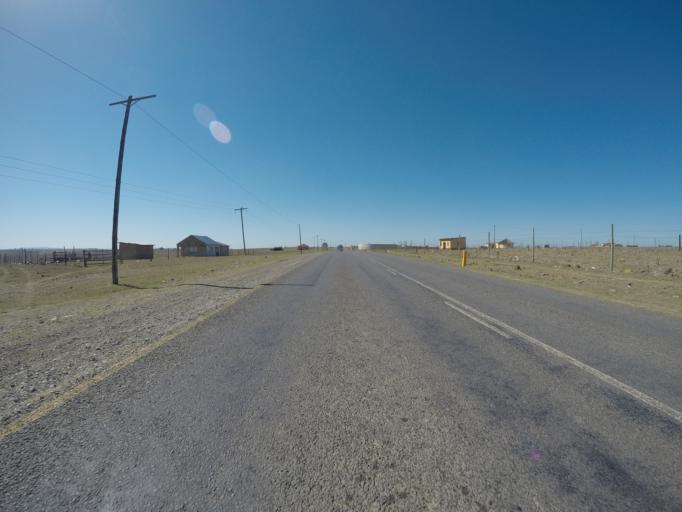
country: ZA
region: Eastern Cape
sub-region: OR Tambo District Municipality
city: Mthatha
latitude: -31.8853
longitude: 28.7601
